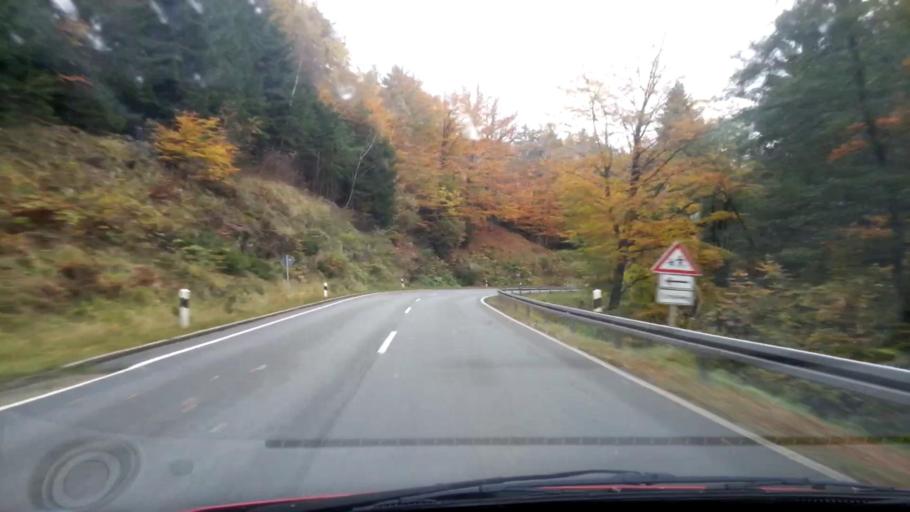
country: DE
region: Bavaria
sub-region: Upper Franconia
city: Warmensteinach
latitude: 49.9618
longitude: 11.7617
